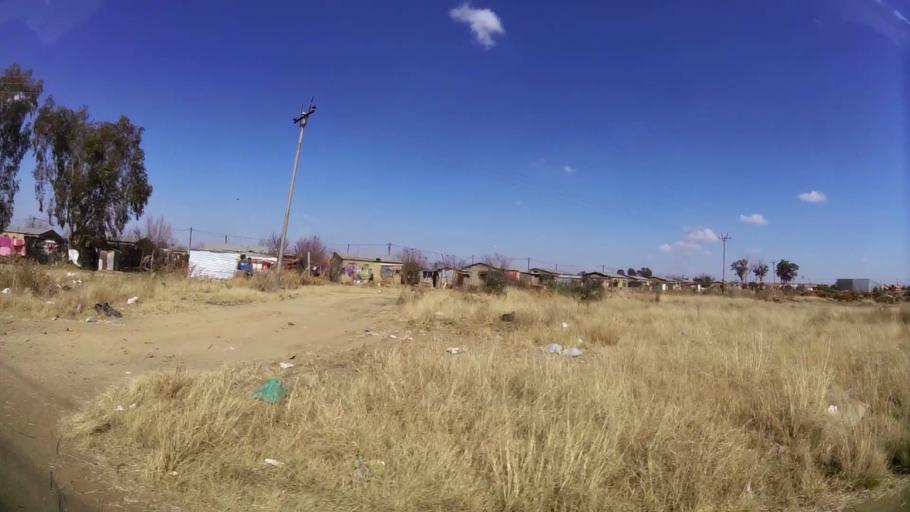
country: ZA
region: Orange Free State
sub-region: Mangaung Metropolitan Municipality
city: Bloemfontein
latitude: -29.1465
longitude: 26.2768
